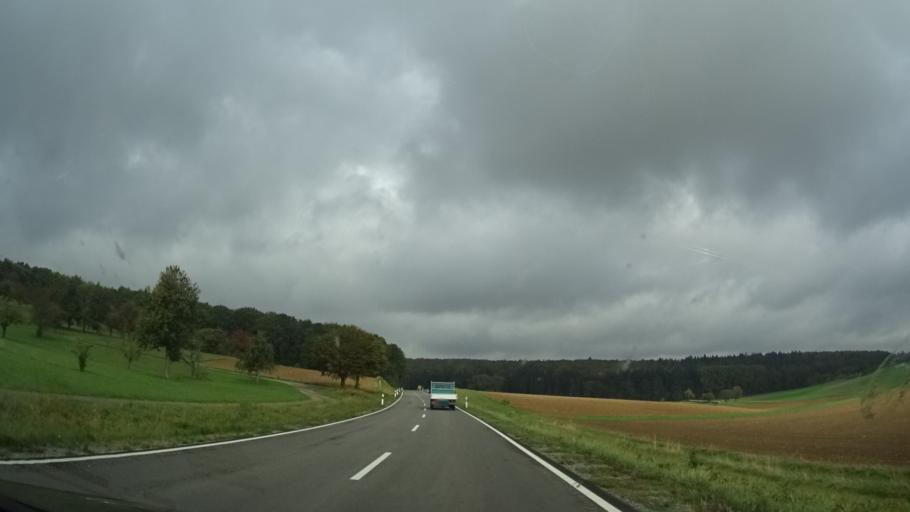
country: DE
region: Baden-Wuerttemberg
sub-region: Karlsruhe Region
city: Konigsbach-Stein
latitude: 48.9841
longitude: 8.6386
